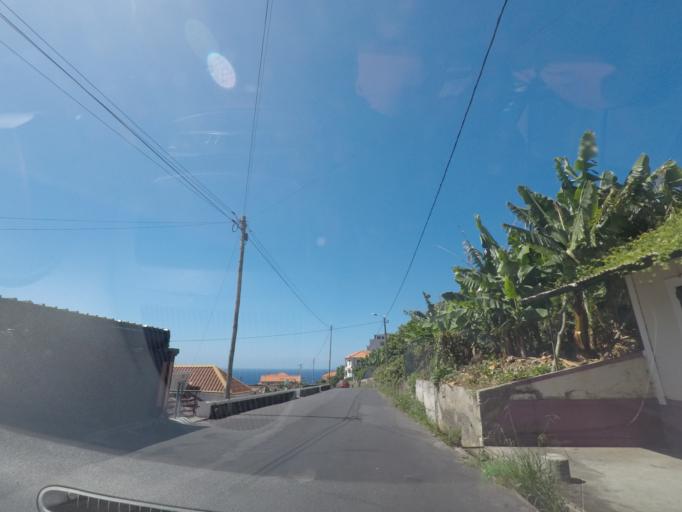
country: PT
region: Madeira
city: Ponta do Sol
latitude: 32.6847
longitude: -17.0964
